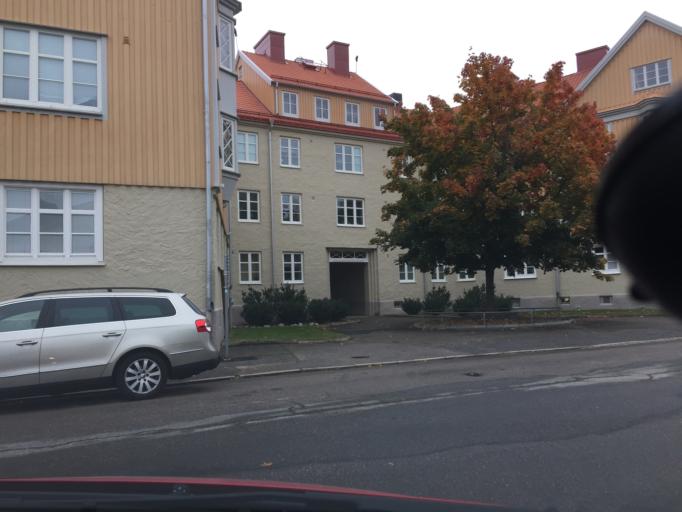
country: SE
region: Vaestra Goetaland
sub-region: Trollhattan
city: Trollhattan
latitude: 58.2845
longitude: 12.2972
